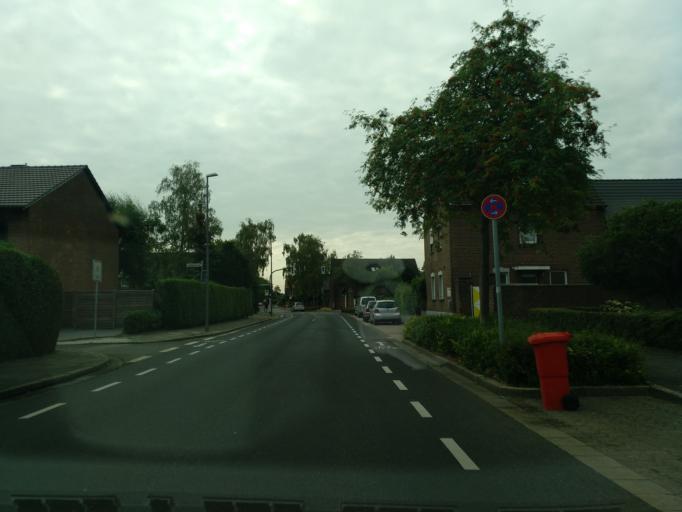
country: DE
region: North Rhine-Westphalia
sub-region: Regierungsbezirk Dusseldorf
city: Krefeld
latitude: 51.2985
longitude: 6.5888
